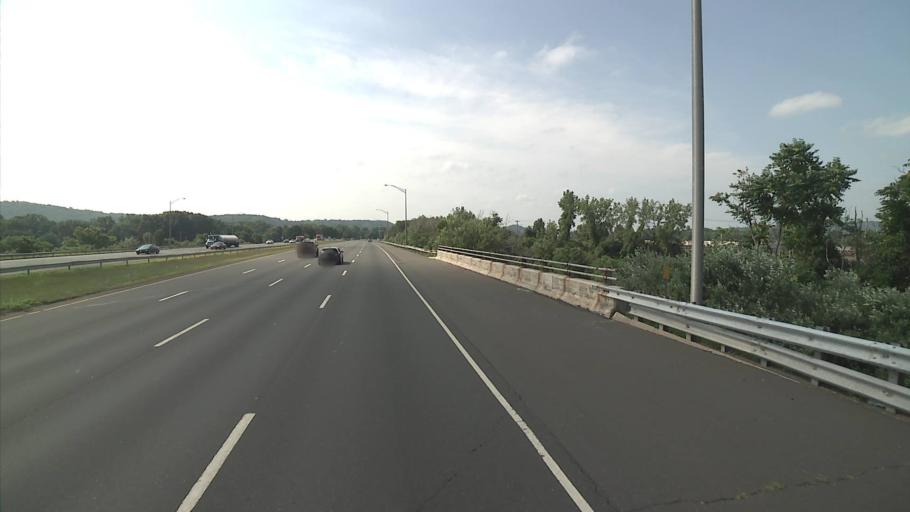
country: US
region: Connecticut
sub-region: New Haven County
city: North Haven
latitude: 41.3544
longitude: -72.8683
